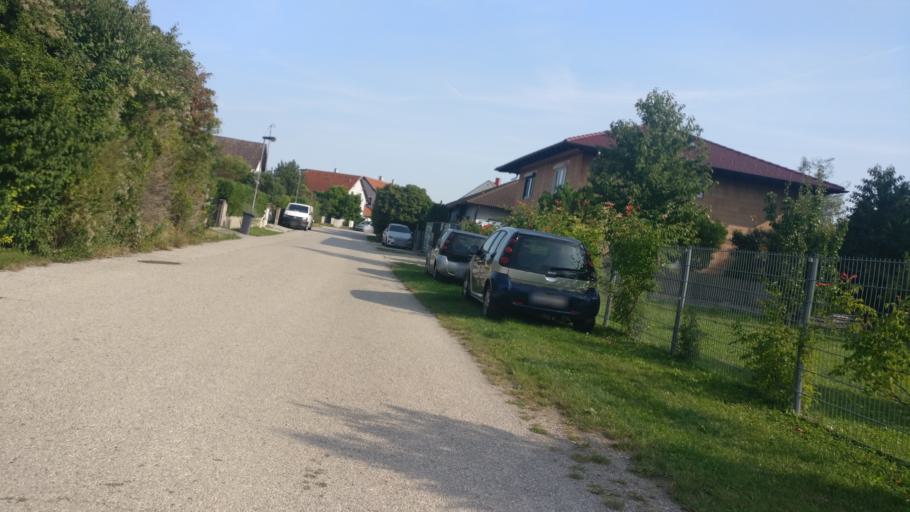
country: AT
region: Lower Austria
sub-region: Politischer Bezirk Baden
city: Ebreichsdorf
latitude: 47.9690
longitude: 16.4084
